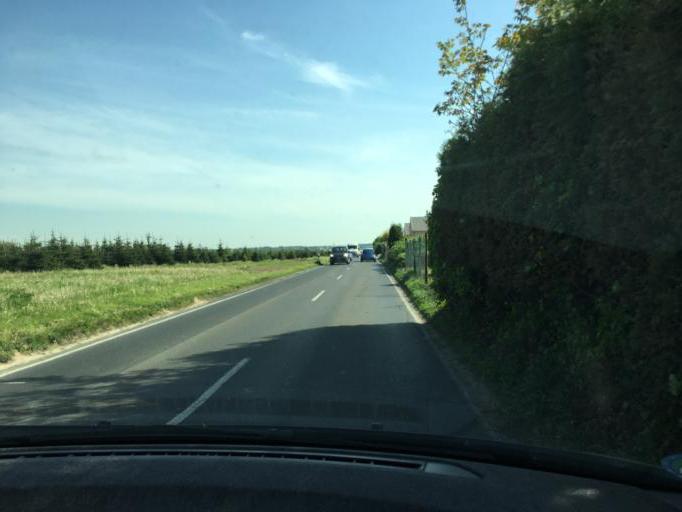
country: DE
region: North Rhine-Westphalia
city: Wesseling
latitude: 50.7893
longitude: 6.9562
